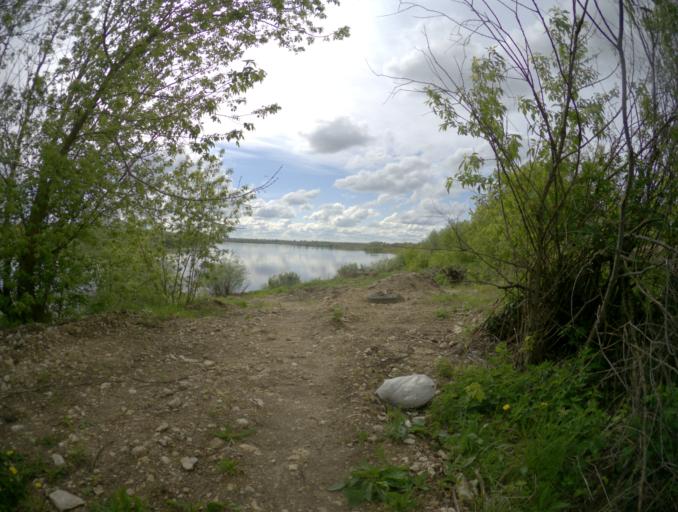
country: RU
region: Rjazan
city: Gus'-Zheleznyy
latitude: 54.9979
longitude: 41.1949
